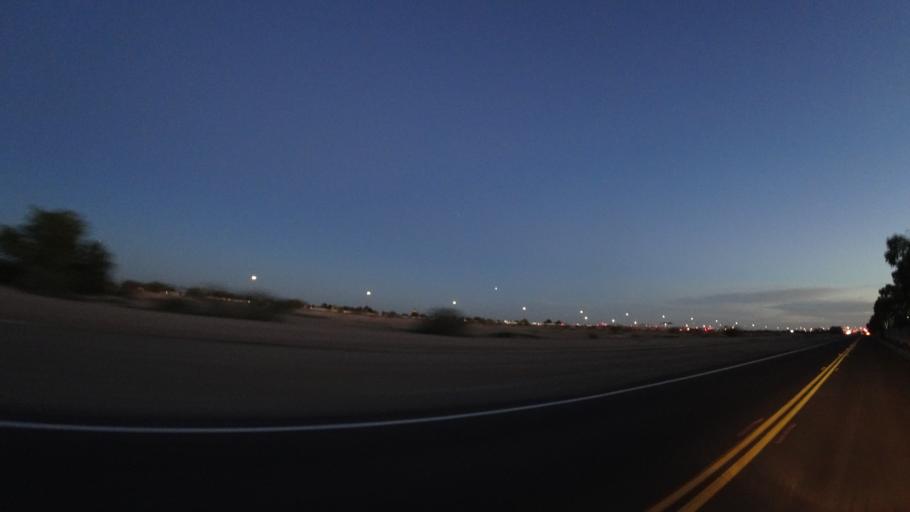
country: US
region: Arizona
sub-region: Maricopa County
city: Scottsdale
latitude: 33.4730
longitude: -111.8919
